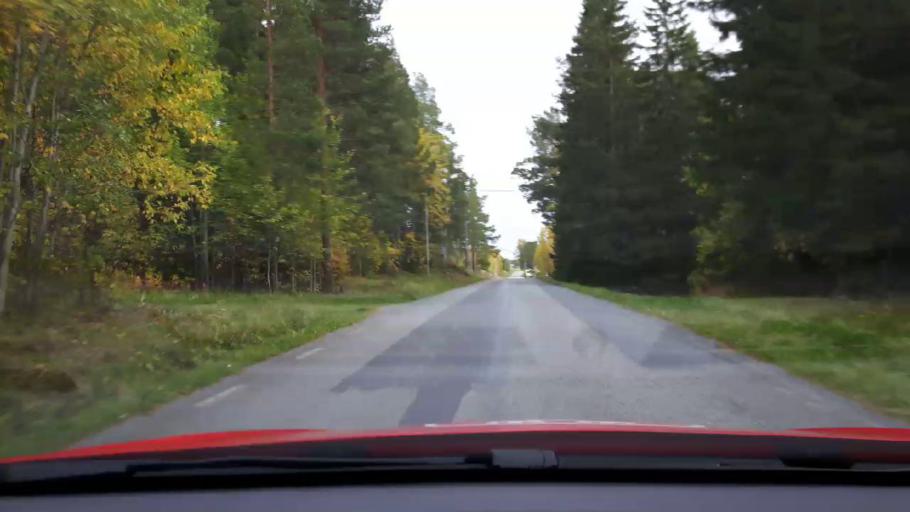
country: SE
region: Jaemtland
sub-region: Krokoms Kommun
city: Valla
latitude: 63.2556
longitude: 14.0230
